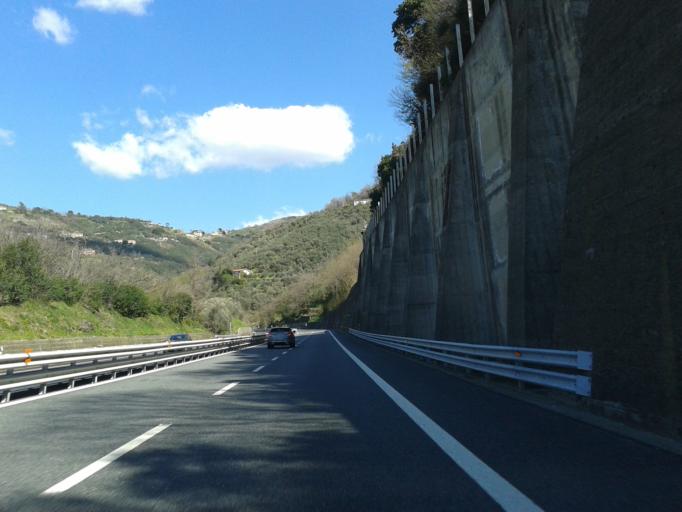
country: IT
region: Liguria
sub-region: Provincia di Genova
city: Cogorno
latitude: 44.2978
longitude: 9.3840
